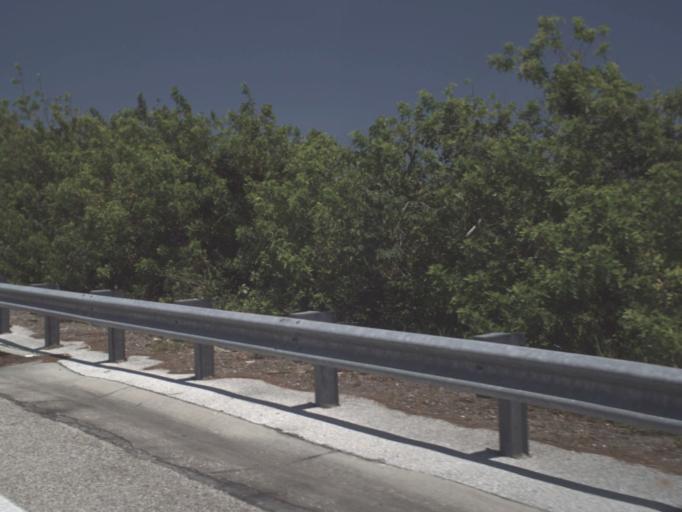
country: US
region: Florida
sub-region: Brevard County
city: Micco
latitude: 27.8838
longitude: -80.5029
